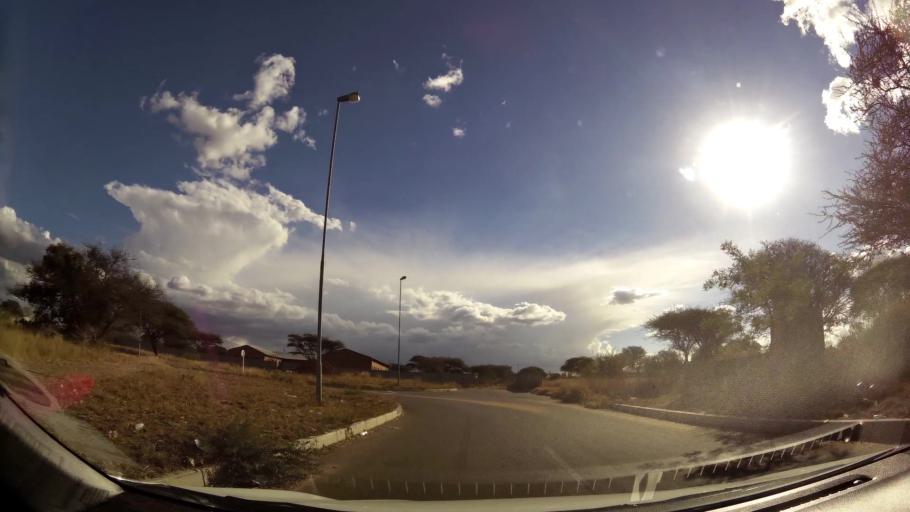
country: ZA
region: Limpopo
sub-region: Capricorn District Municipality
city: Polokwane
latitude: -23.9352
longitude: 29.4461
